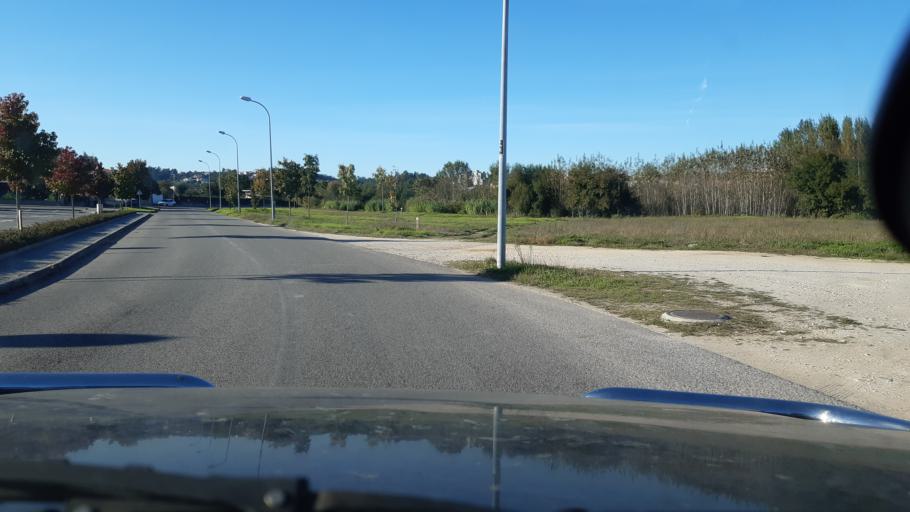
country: PT
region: Aveiro
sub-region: Agueda
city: Agueda
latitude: 40.5627
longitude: -8.4430
